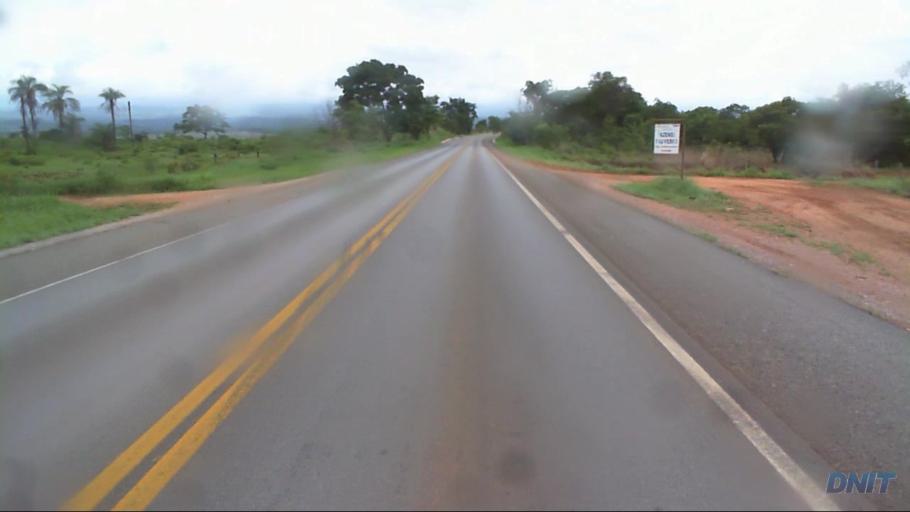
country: BR
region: Goias
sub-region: Padre Bernardo
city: Padre Bernardo
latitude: -15.1816
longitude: -48.4278
